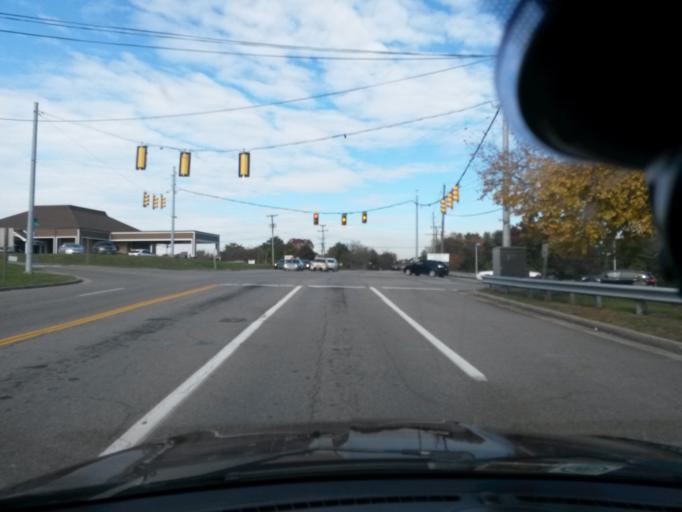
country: US
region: Virginia
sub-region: Roanoke County
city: Narrows
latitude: 37.2282
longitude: -79.9806
